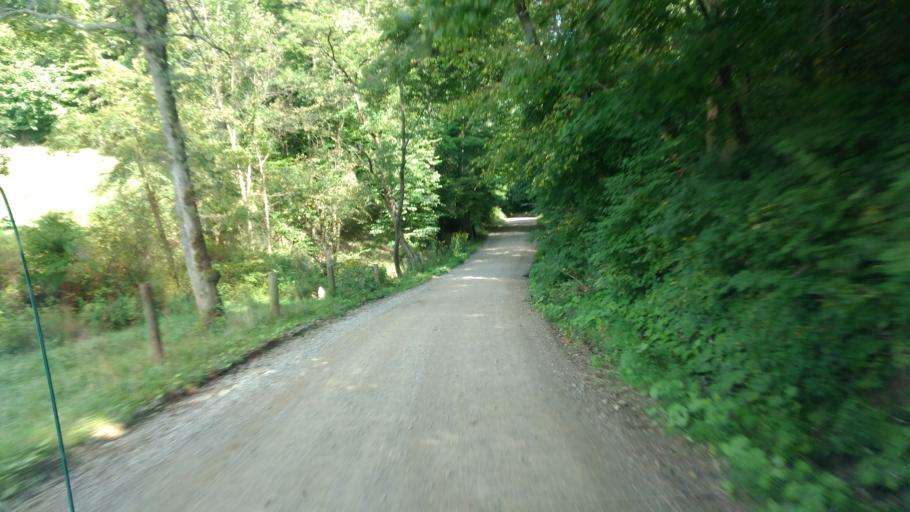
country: US
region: Ohio
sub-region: Holmes County
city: Millersburg
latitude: 40.6489
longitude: -81.9005
